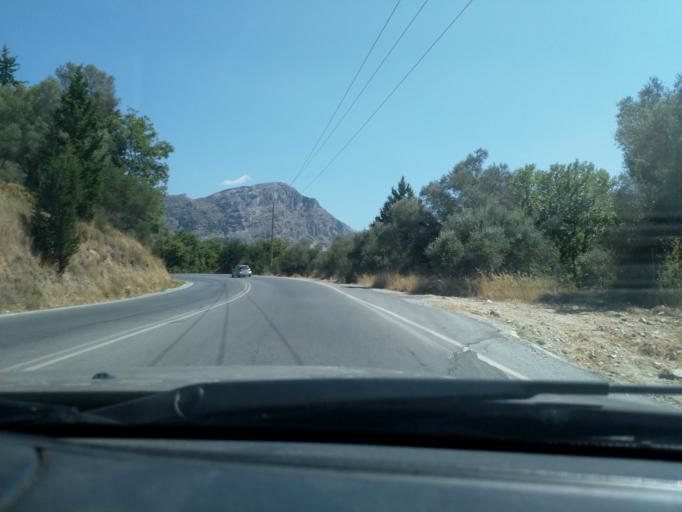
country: GR
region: Crete
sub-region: Nomos Rethymnis
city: Agia Foteini
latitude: 35.2203
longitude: 24.5157
